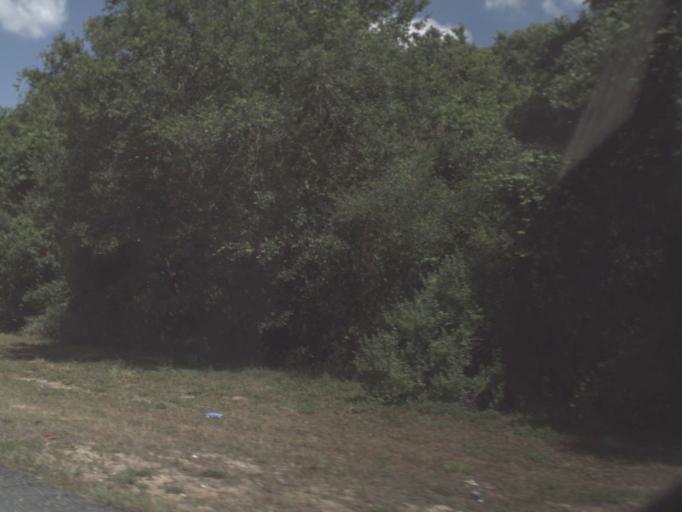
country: US
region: Florida
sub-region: Lake County
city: Astor
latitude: 29.1755
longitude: -81.6975
